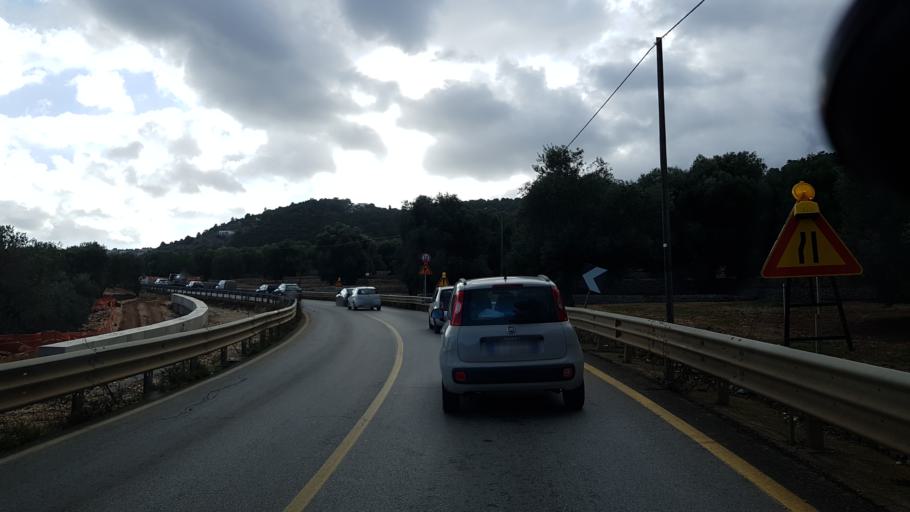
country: IT
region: Apulia
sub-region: Provincia di Brindisi
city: Lamie di Olimpie-Selva
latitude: 40.8208
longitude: 17.3455
